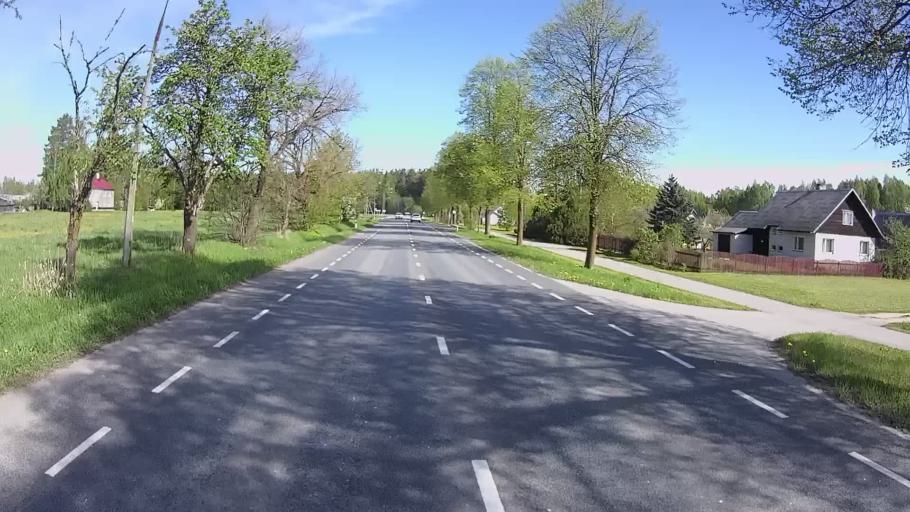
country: EE
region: Polvamaa
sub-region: Polva linn
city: Polva
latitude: 58.2153
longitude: 27.0699
